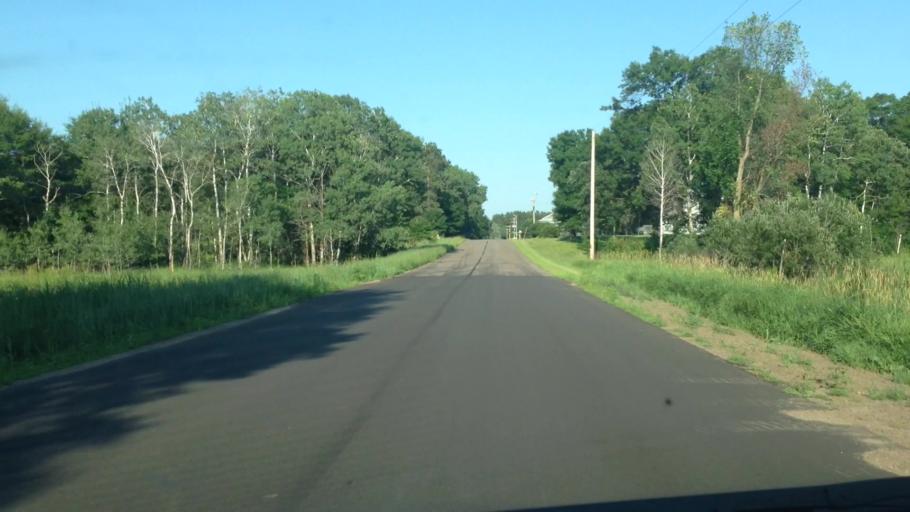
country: US
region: Minnesota
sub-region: Sherburne County
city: Big Lake
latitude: 45.4440
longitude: -93.7435
